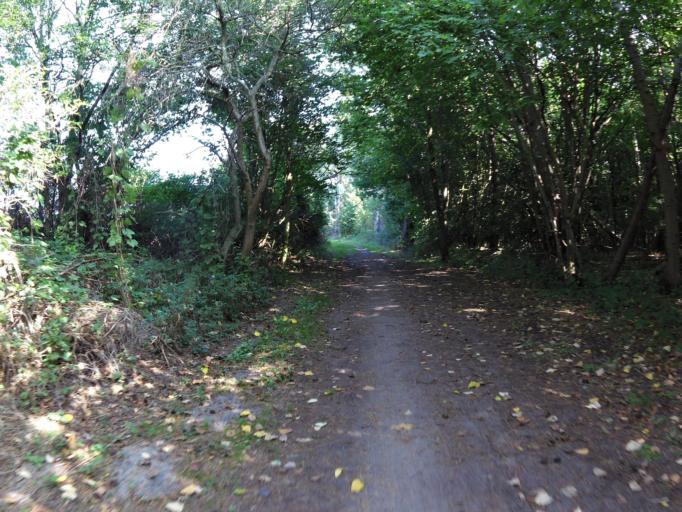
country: DE
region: Mecklenburg-Vorpommern
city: Loddin
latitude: 53.9617
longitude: 14.0434
